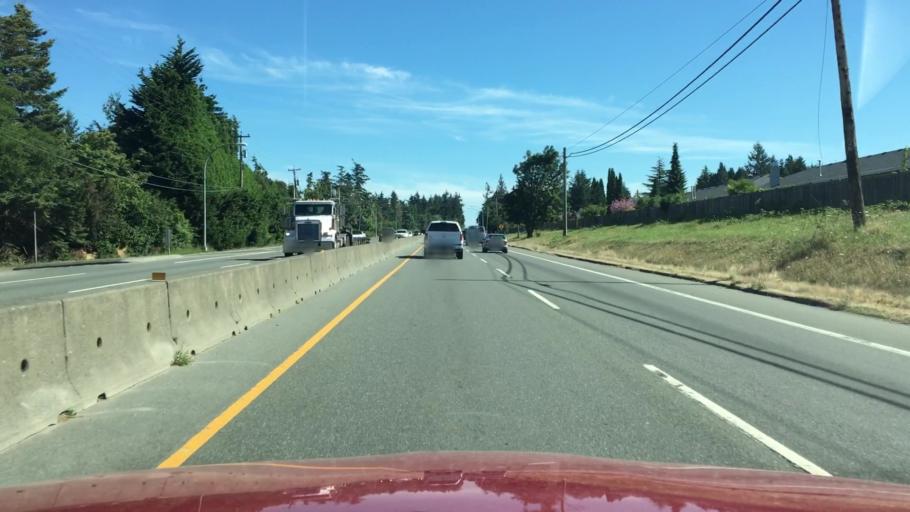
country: CA
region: British Columbia
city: North Saanich
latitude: 48.5569
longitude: -123.3936
